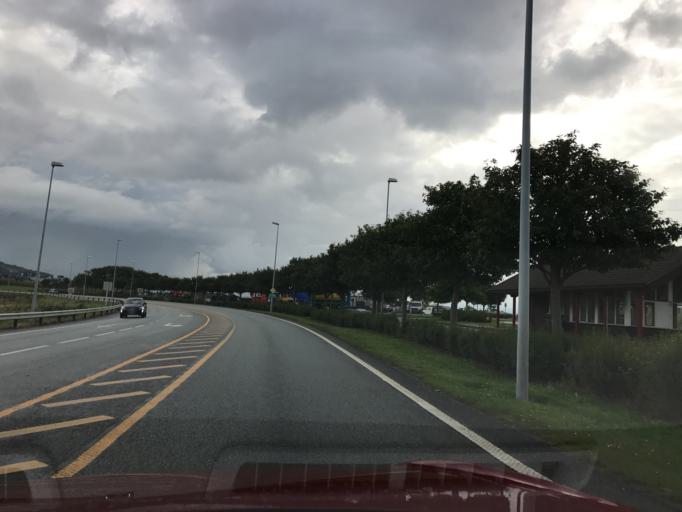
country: NO
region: Rogaland
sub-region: Rennesoy
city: Vikevag
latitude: 59.0564
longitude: 5.6723
